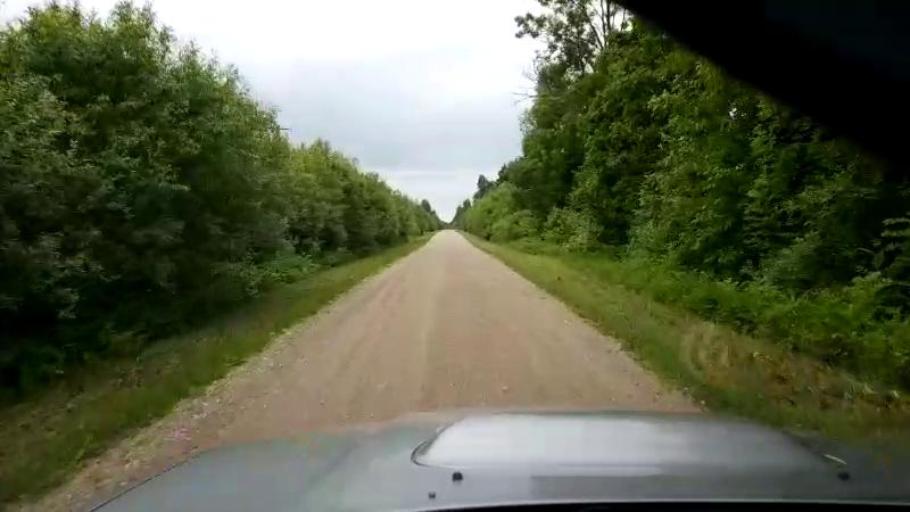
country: EE
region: Paernumaa
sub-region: Halinga vald
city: Parnu-Jaagupi
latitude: 58.5611
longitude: 24.5635
